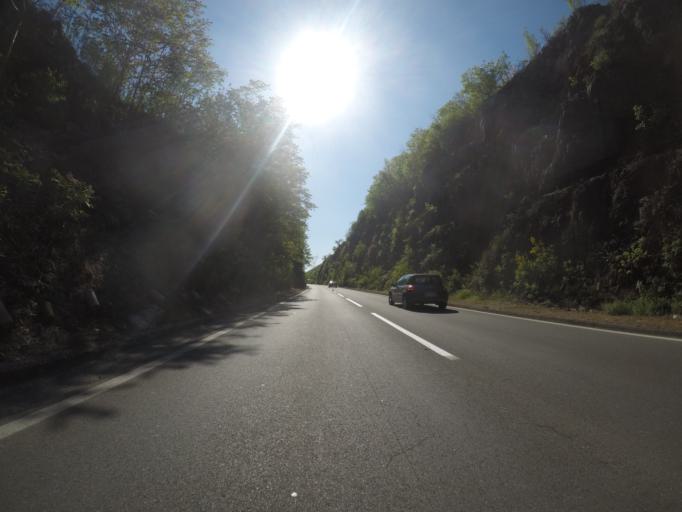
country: ME
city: Spuz
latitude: 42.4569
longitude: 19.1827
